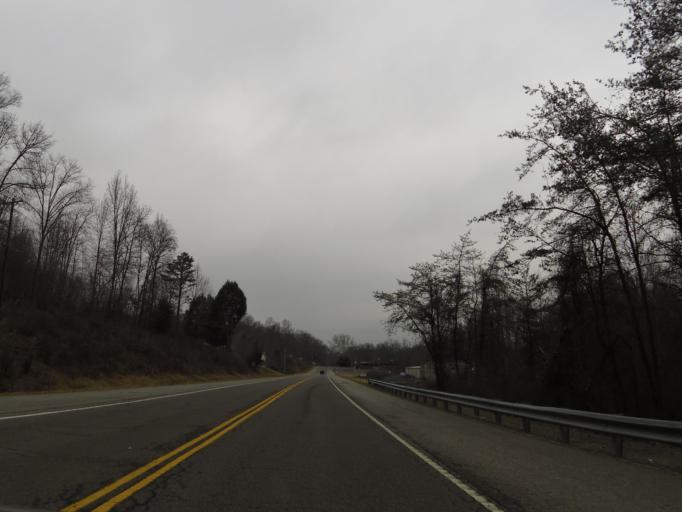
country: US
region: Tennessee
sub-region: Morgan County
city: Wartburg
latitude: 36.2349
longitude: -84.6705
